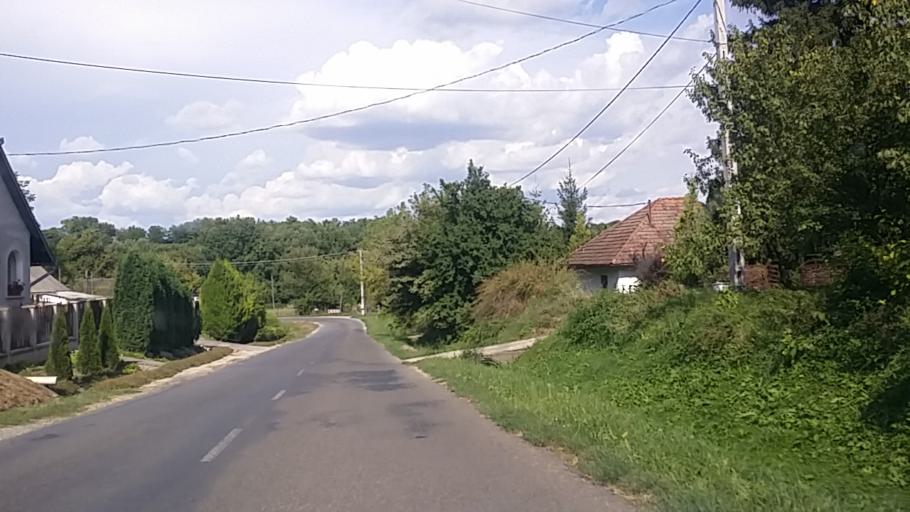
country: HU
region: Tolna
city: Gyonk
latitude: 46.5492
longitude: 18.4795
